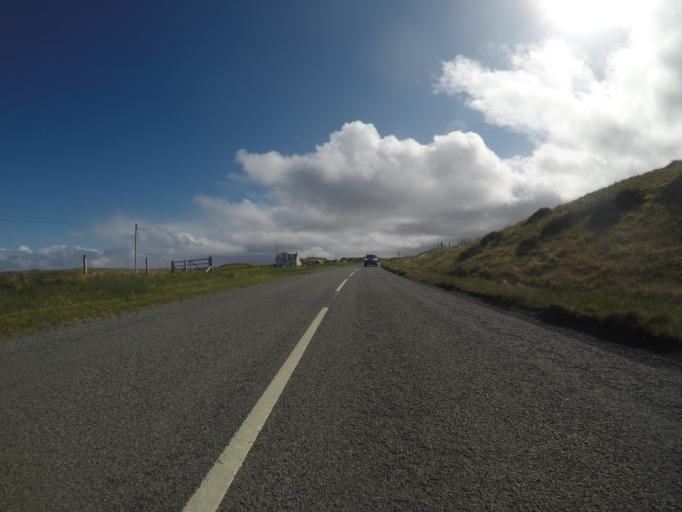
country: GB
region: Scotland
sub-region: Highland
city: Portree
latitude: 57.5754
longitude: -6.1550
